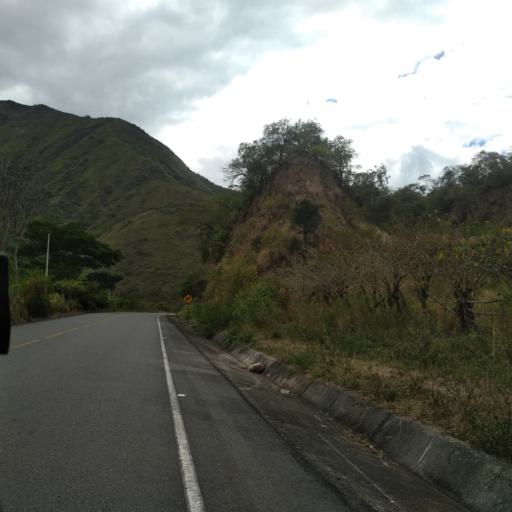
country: PE
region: Cajamarca
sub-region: Provincia de San Ignacio
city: Chirinos
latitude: -5.2357
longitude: -78.8606
